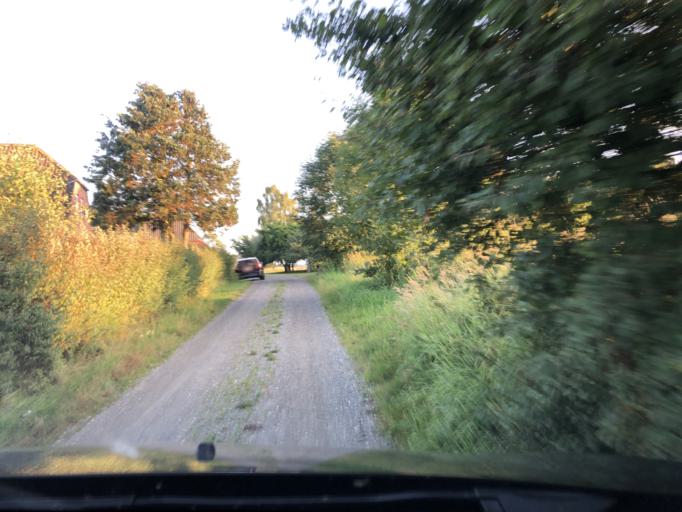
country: DK
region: South Denmark
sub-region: Vejle Kommune
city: Brejning
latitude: 55.6493
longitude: 9.7191
